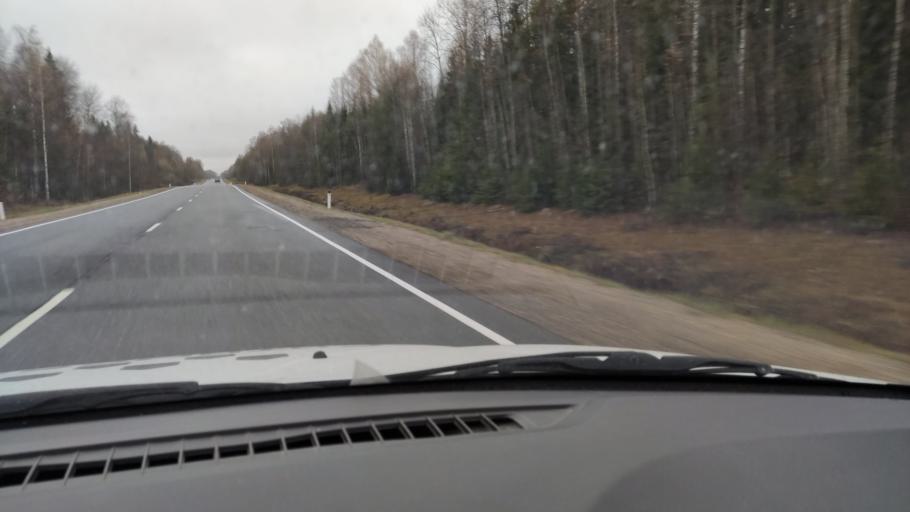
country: RU
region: Kirov
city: Chernaya Kholunitsa
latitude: 58.7794
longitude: 51.9179
